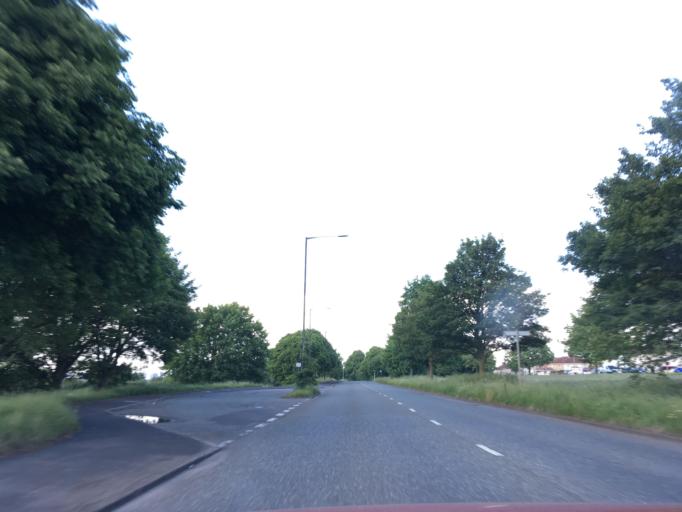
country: GB
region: England
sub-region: North Somerset
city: Dundry
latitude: 51.4249
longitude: -2.6218
